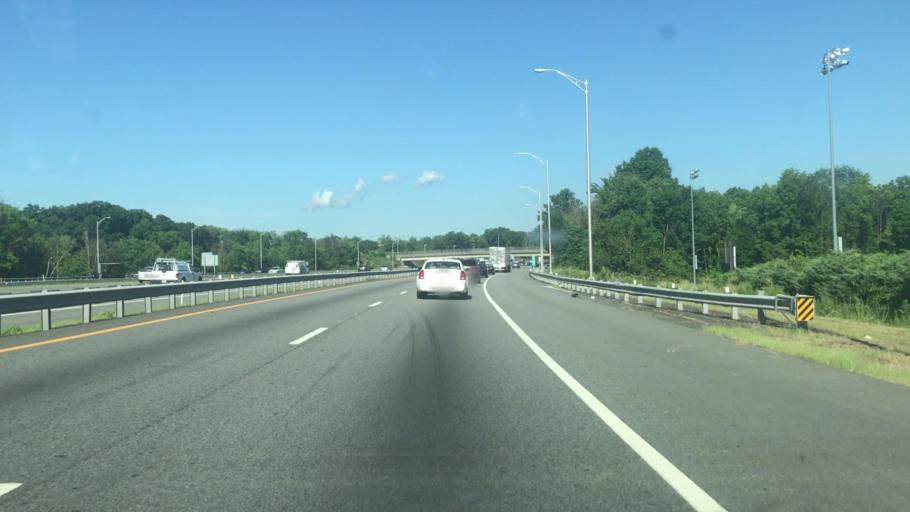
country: US
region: New Jersey
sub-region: Morris County
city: Parsippany
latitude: 40.8609
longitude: -74.3952
